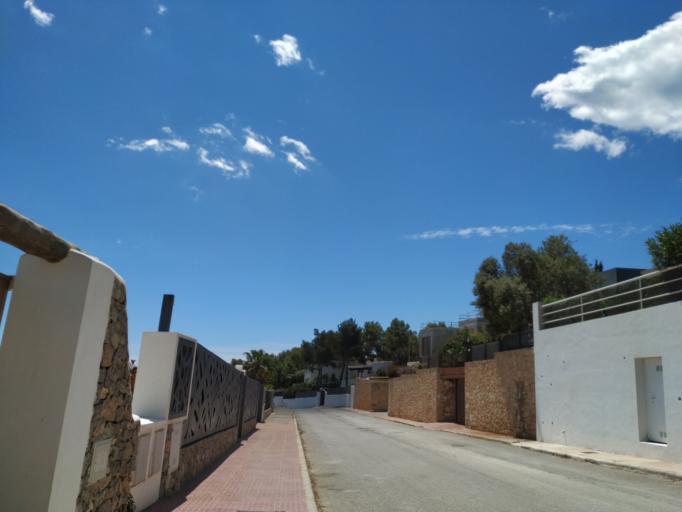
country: ES
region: Balearic Islands
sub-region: Illes Balears
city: Ibiza
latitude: 38.9185
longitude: 1.4734
